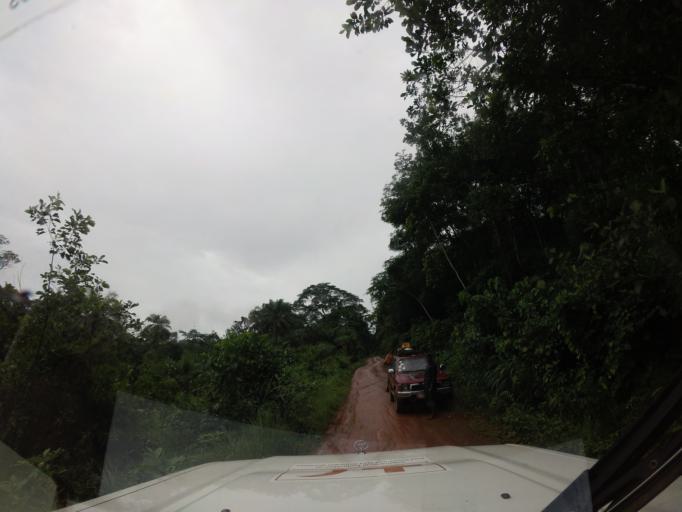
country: SL
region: Eastern Province
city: Kenema
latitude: 7.7274
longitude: -11.1887
